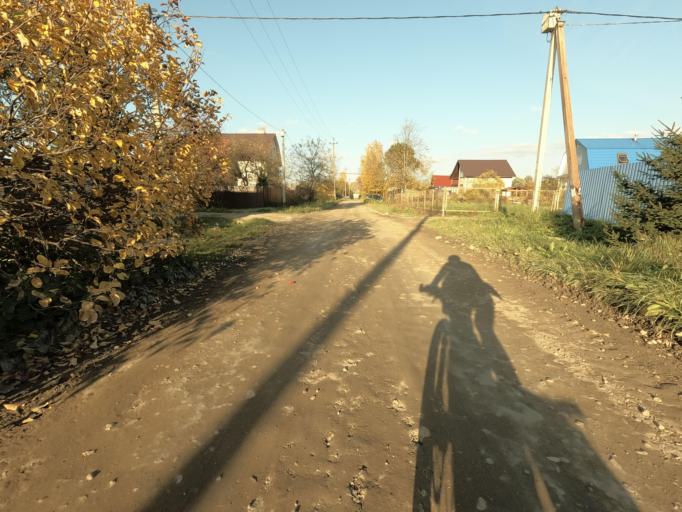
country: RU
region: Leningrad
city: Mga
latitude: 59.7521
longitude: 31.0567
